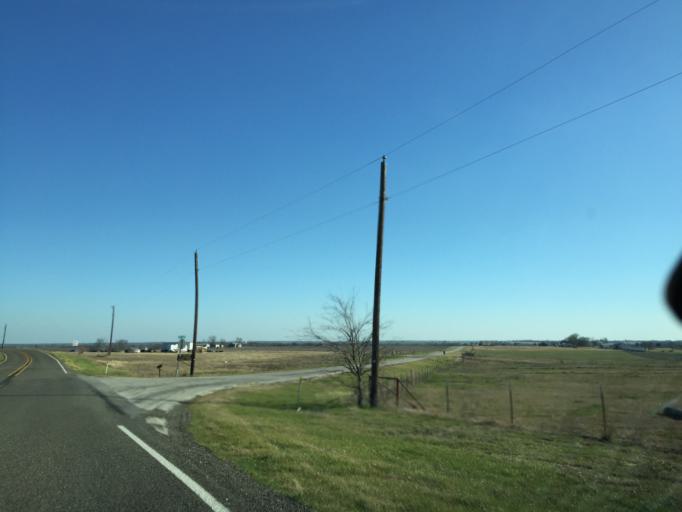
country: US
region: Texas
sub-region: Milam County
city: Thorndale
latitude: 30.5552
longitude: -97.2995
